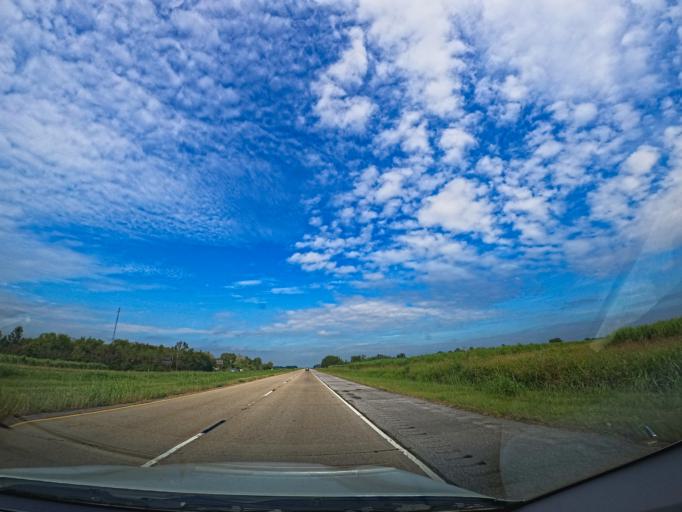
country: US
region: Louisiana
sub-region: Saint Mary Parish
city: Franklin
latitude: 29.7291
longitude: -91.4146
